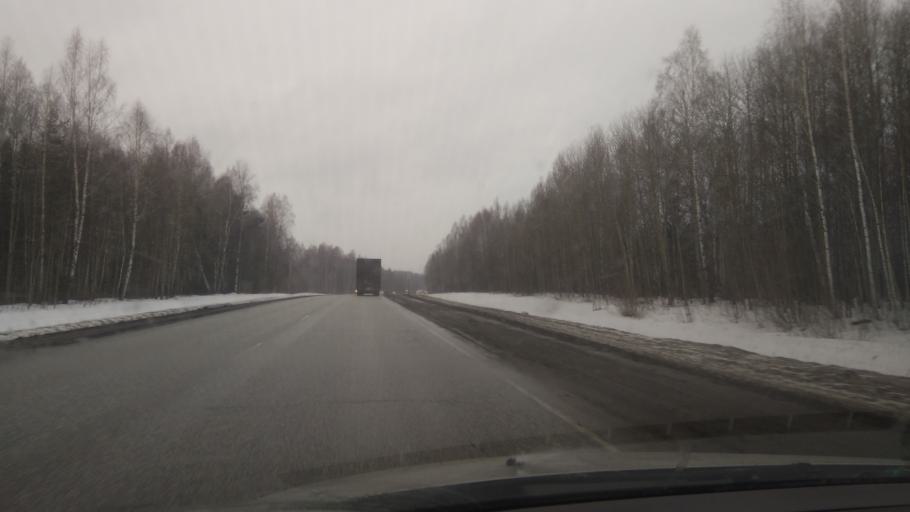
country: RU
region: Perm
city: Kungur
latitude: 57.4299
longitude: 56.8301
